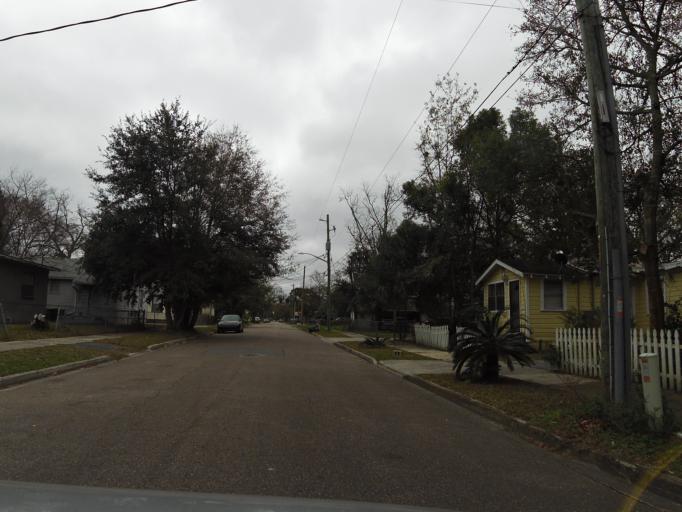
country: US
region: Florida
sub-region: Duval County
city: Jacksonville
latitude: 30.3593
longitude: -81.6893
